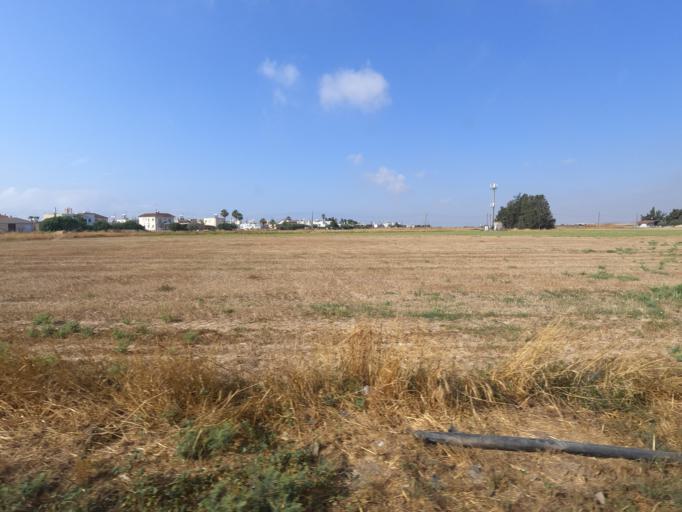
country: CY
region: Larnaka
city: Dhromolaxia
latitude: 34.8762
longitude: 33.5813
